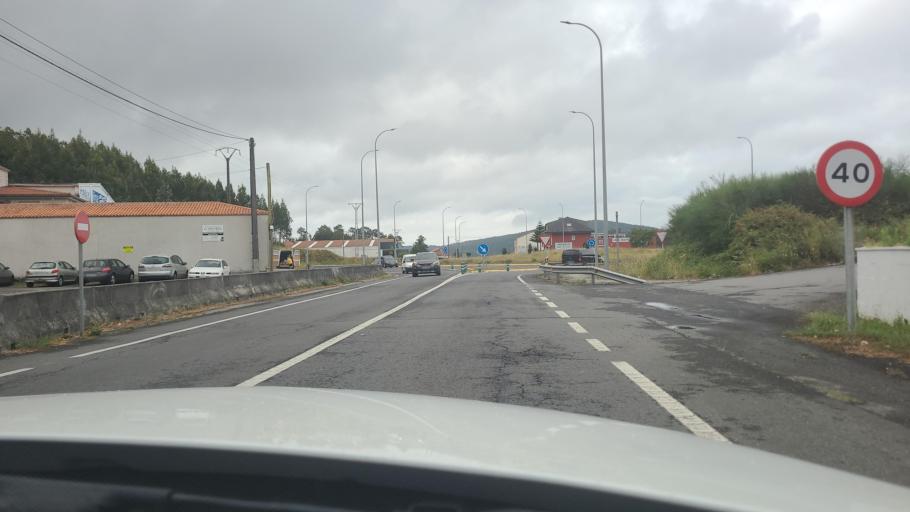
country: ES
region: Galicia
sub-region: Provincia da Coruna
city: Cee
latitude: 42.9785
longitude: -9.1882
